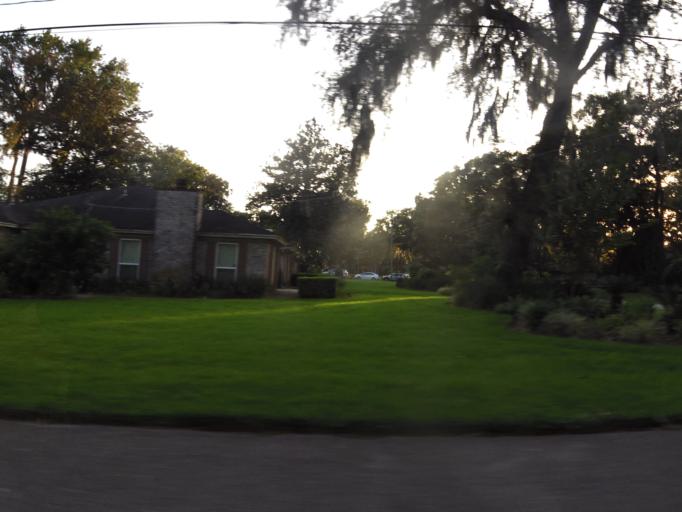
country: US
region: Florida
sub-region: Clay County
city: Orange Park
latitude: 30.1997
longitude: -81.6345
